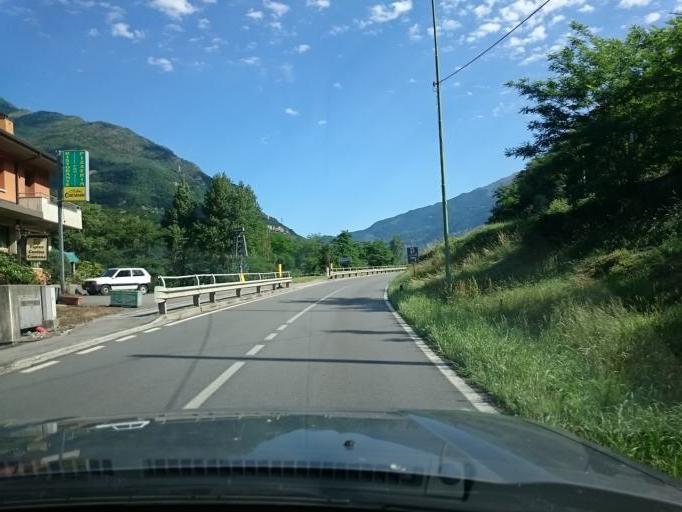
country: IT
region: Lombardy
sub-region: Provincia di Brescia
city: Capo di Ponte
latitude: 46.0217
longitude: 10.3451
